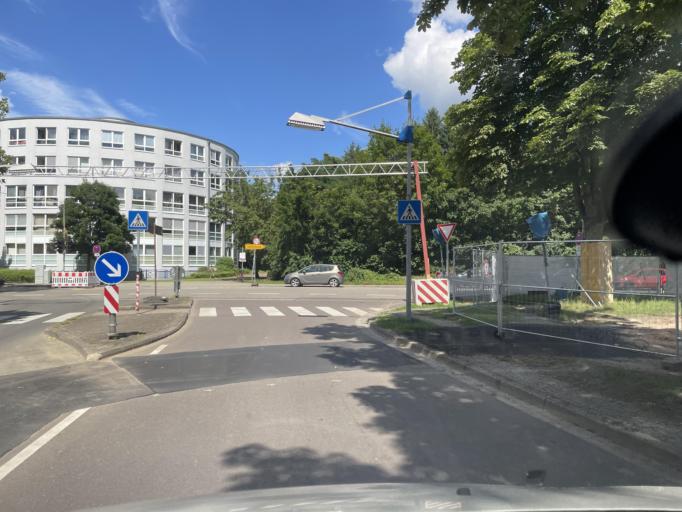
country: DE
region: Saarland
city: Saarbrucken
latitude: 49.2323
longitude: 7.0138
